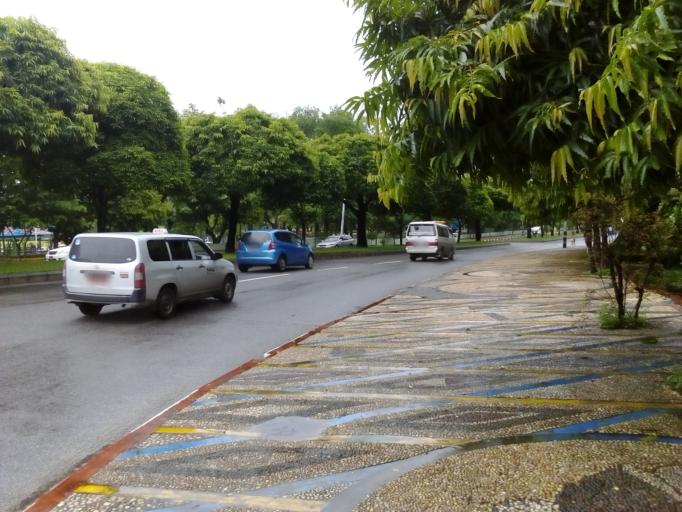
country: MM
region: Yangon
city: Yangon
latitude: 16.7945
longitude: 96.1469
